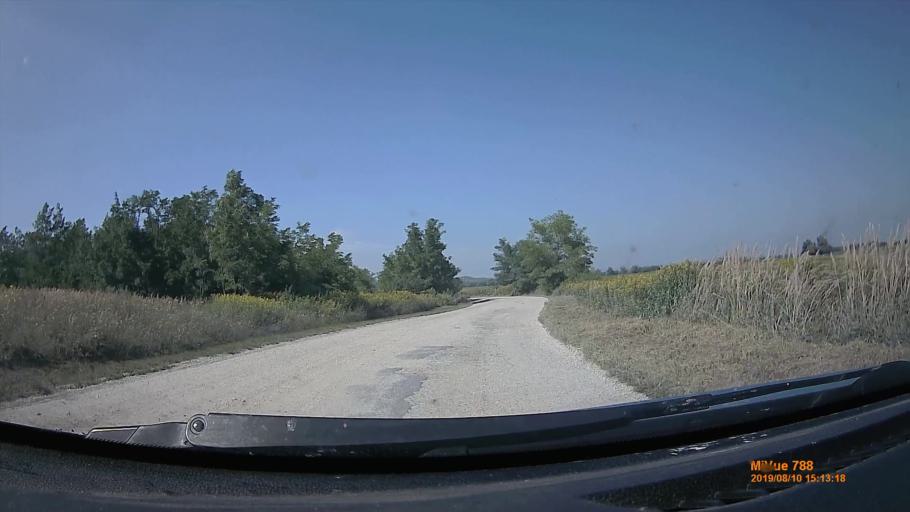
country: HU
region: Somogy
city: Fonyod
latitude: 46.6916
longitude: 17.5615
